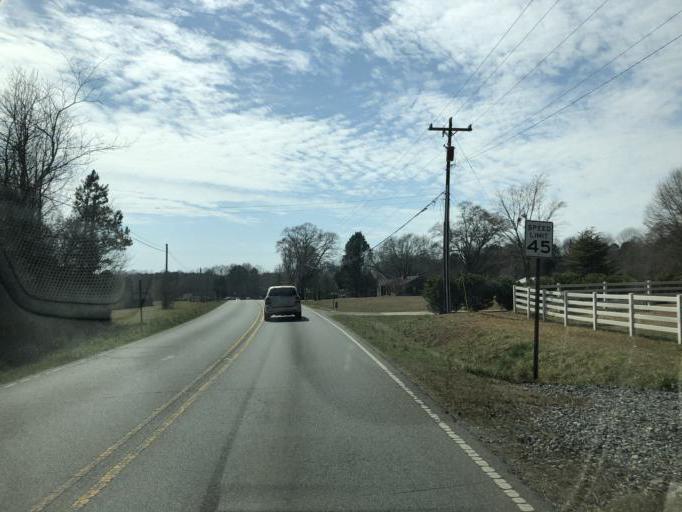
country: US
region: North Carolina
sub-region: Gaston County
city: Stanley
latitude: 35.3399
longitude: -81.1098
